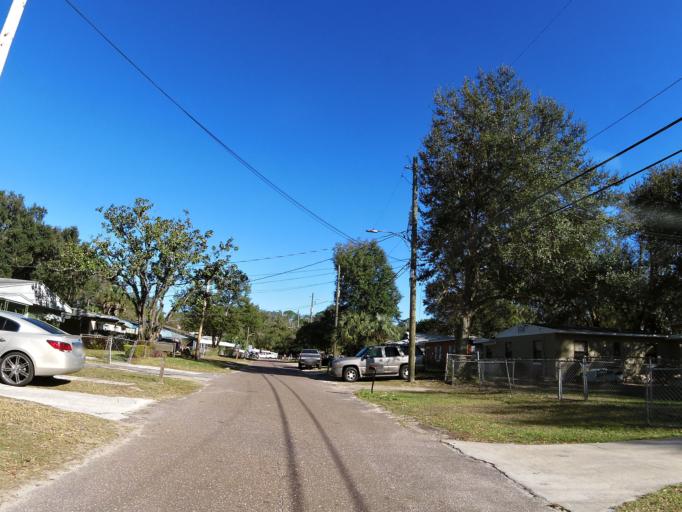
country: US
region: Florida
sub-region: Duval County
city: Jacksonville
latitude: 30.2823
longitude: -81.6455
